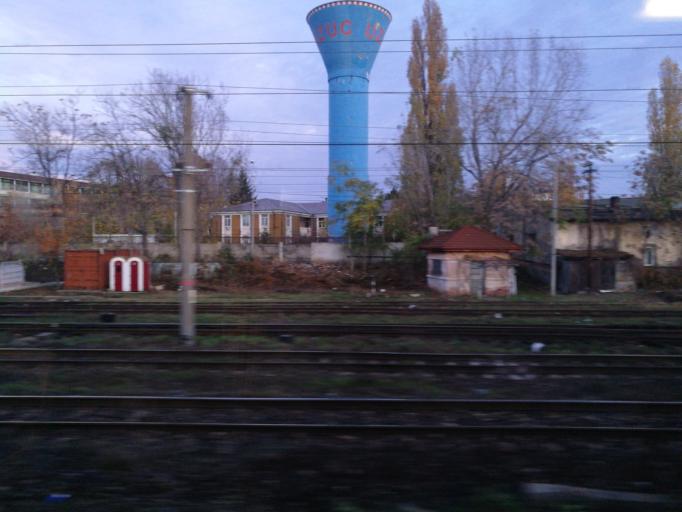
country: RO
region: Prahova
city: Ploiesti
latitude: 44.9232
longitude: 26.0216
